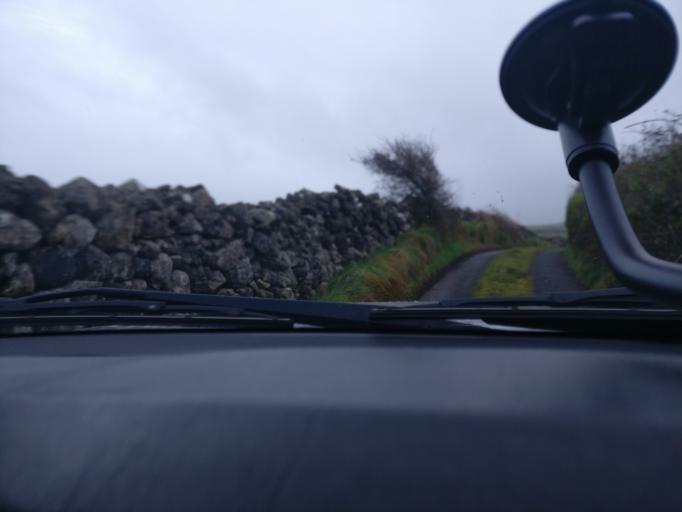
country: IE
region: Connaught
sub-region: County Galway
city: Loughrea
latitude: 53.2119
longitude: -8.5462
